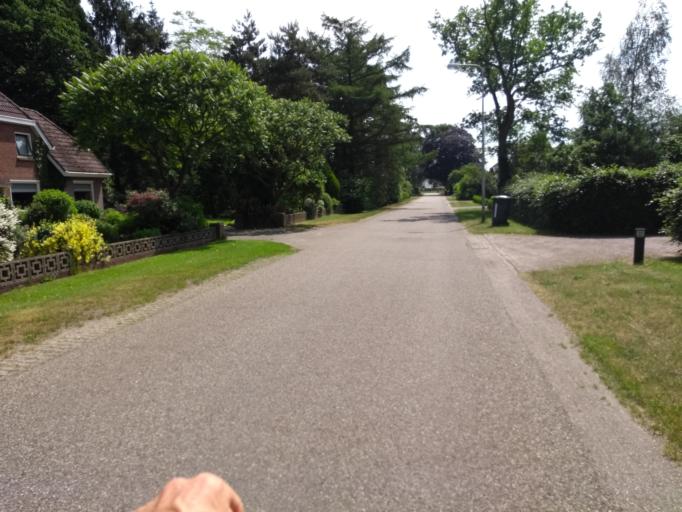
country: NL
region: Overijssel
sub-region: Gemeente Almelo
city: Almelo
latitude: 52.3732
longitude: 6.7178
